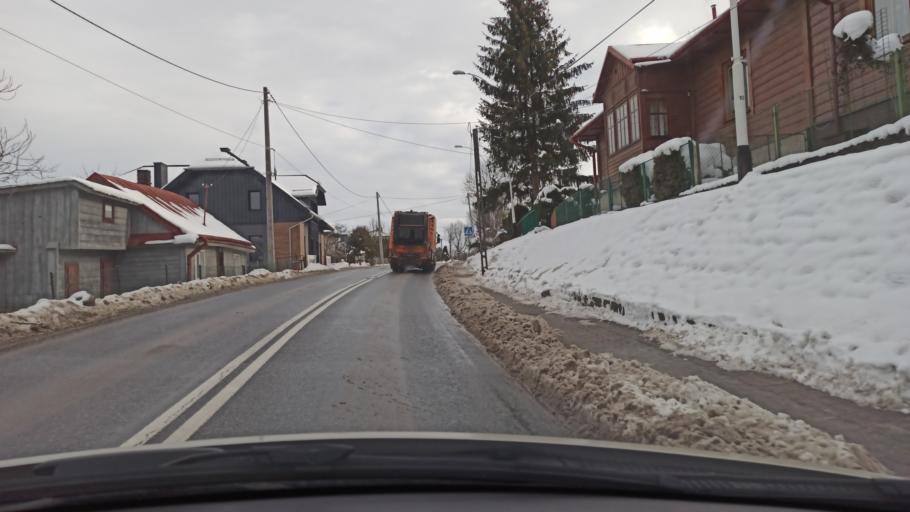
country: PL
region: Subcarpathian Voivodeship
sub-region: Powiat lezajski
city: Lezajsk
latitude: 50.2527
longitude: 22.4268
